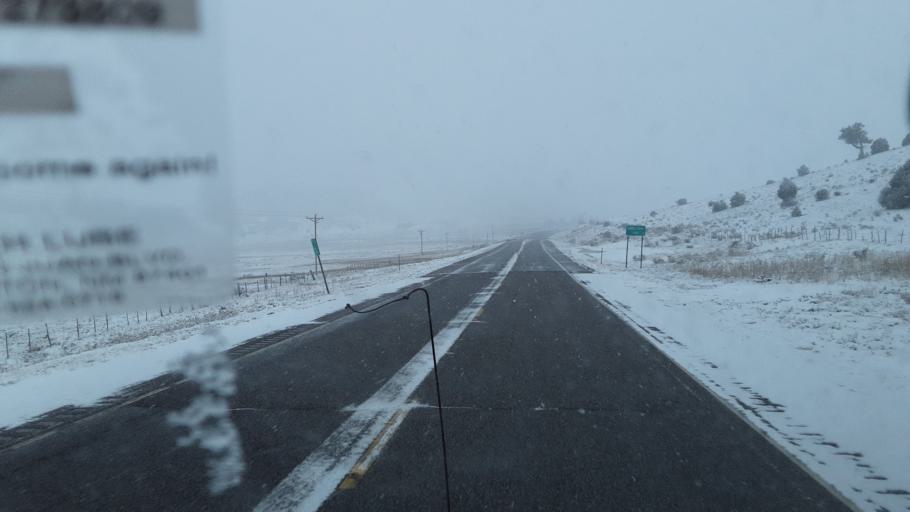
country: US
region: New Mexico
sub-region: Rio Arriba County
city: Chama
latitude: 36.9021
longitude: -106.7872
